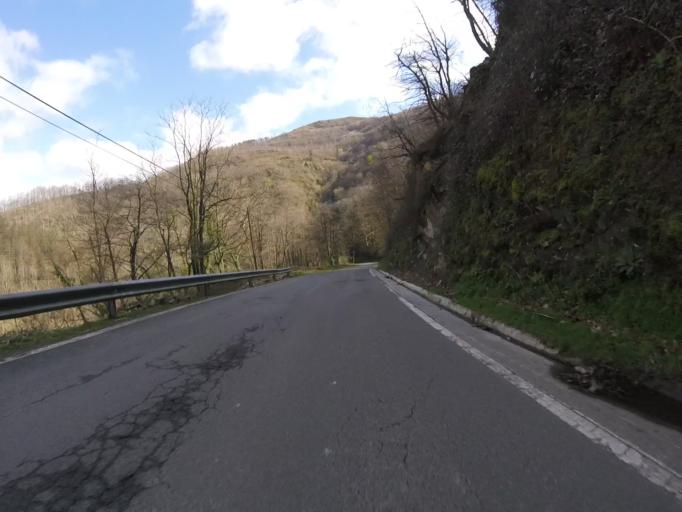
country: ES
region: Navarre
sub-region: Provincia de Navarra
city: Goizueta
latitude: 43.1530
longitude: -1.8491
